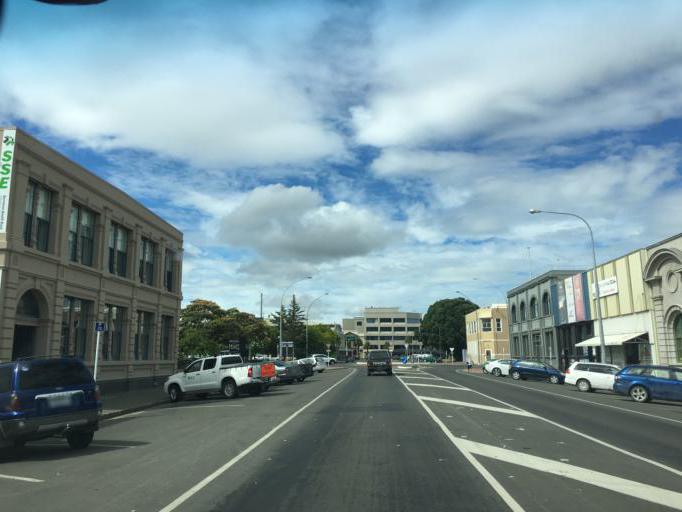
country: NZ
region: Gisborne
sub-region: Gisborne District
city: Gisborne
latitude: -38.6696
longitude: 178.0261
